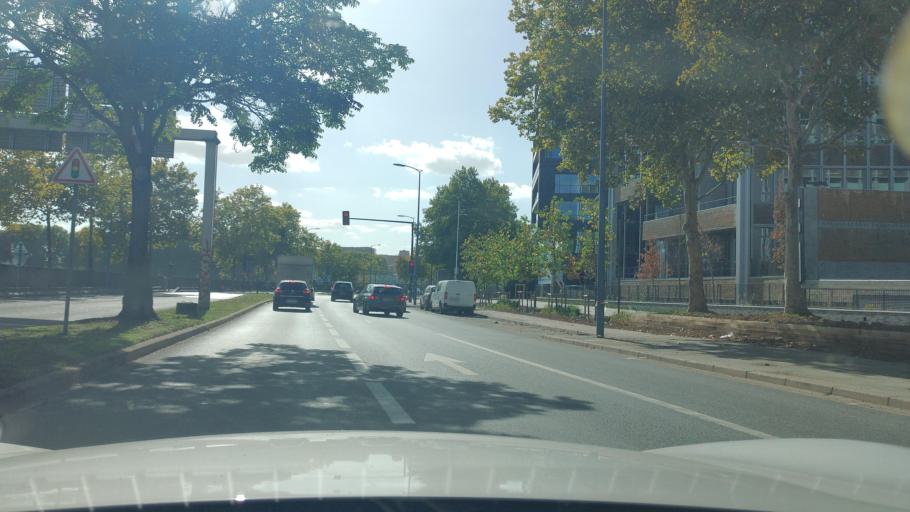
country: FR
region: Ile-de-France
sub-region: Departement des Hauts-de-Seine
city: Villeneuve-la-Garenne
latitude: 48.9199
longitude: 2.3205
